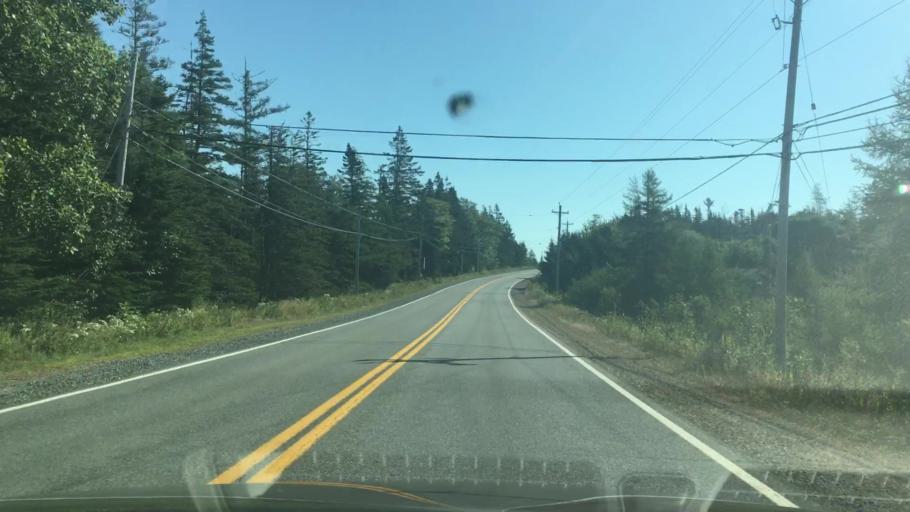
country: CA
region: Nova Scotia
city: Cole Harbour
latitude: 44.7795
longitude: -63.0034
